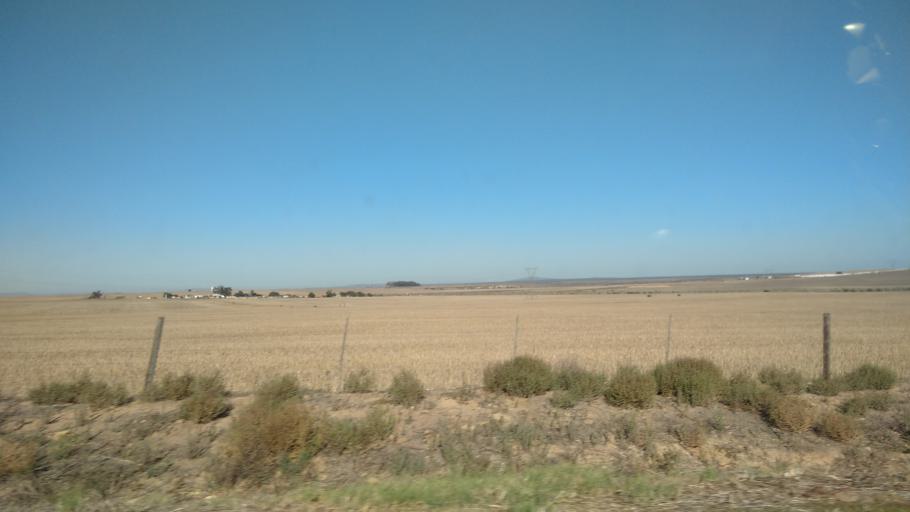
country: ZA
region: Western Cape
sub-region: West Coast District Municipality
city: Moorreesburg
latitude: -33.1523
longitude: 18.4659
